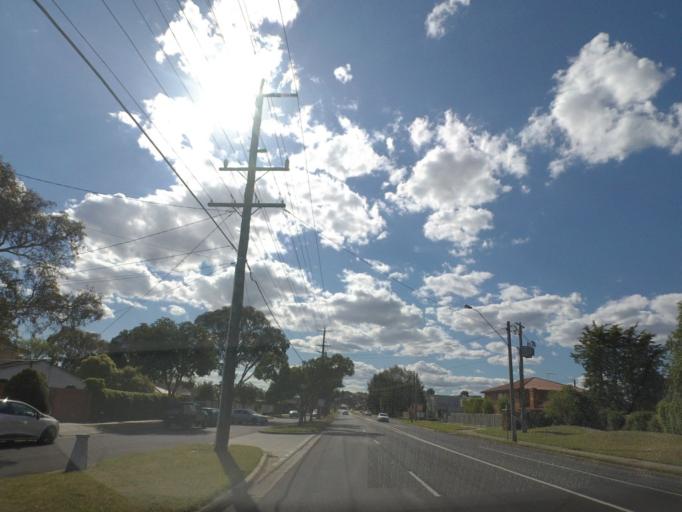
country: AU
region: Victoria
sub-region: Kingston
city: Dingley Village
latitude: -37.9758
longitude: 145.1226
